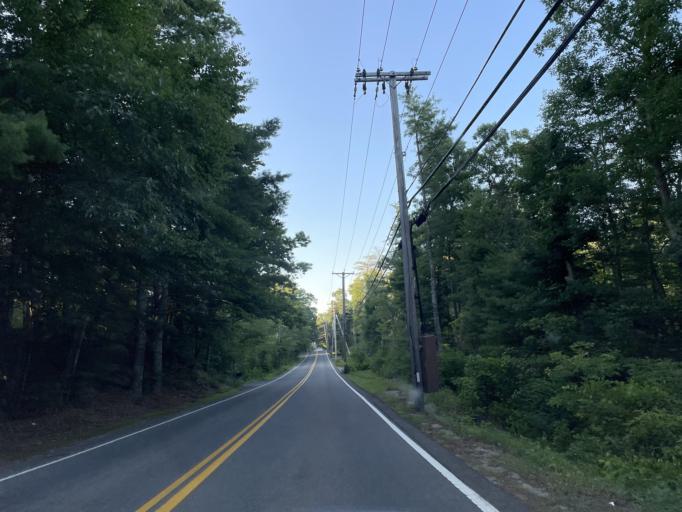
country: US
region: Massachusetts
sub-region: Plymouth County
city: Halifax
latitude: 42.0348
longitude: -70.8446
